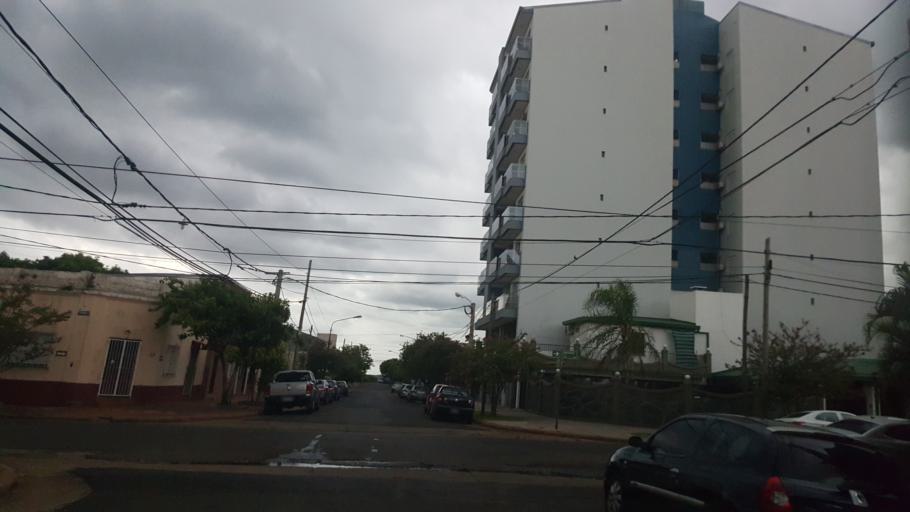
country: AR
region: Misiones
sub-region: Departamento de Capital
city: Posadas
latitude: -27.3554
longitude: -55.8952
